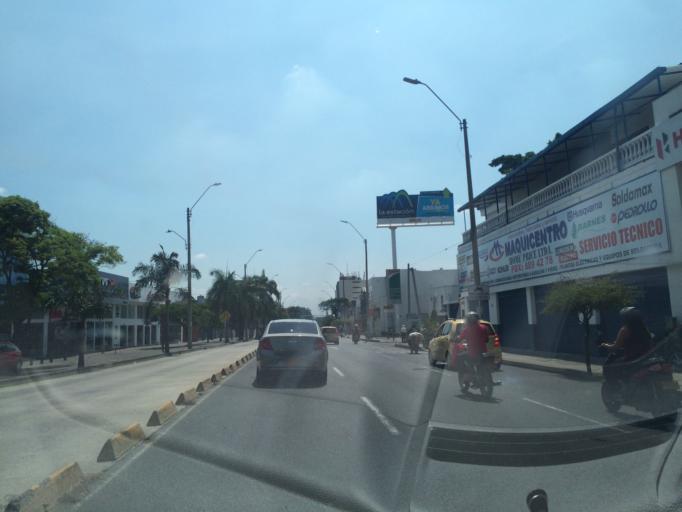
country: CO
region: Valle del Cauca
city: Cali
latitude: 3.4586
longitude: -76.5254
